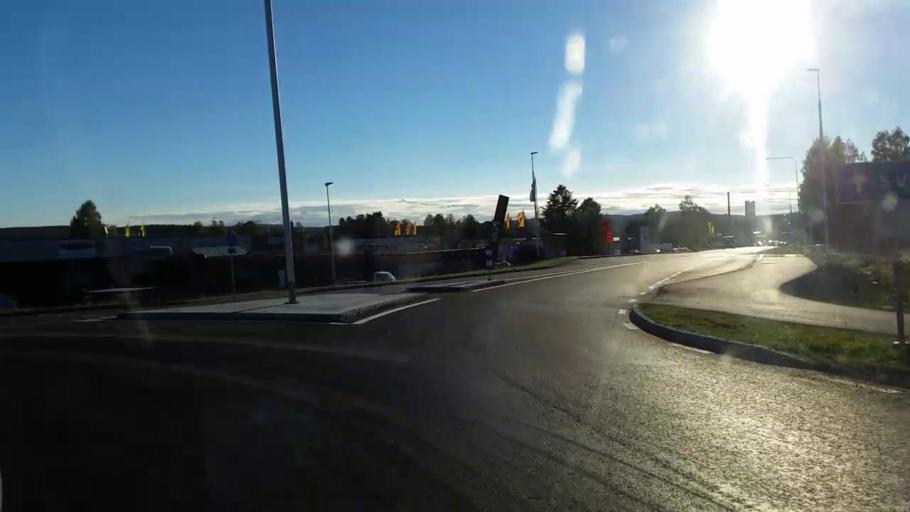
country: SE
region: Gaevleborg
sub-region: Ljusdals Kommun
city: Ljusdal
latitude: 61.8254
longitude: 16.1183
